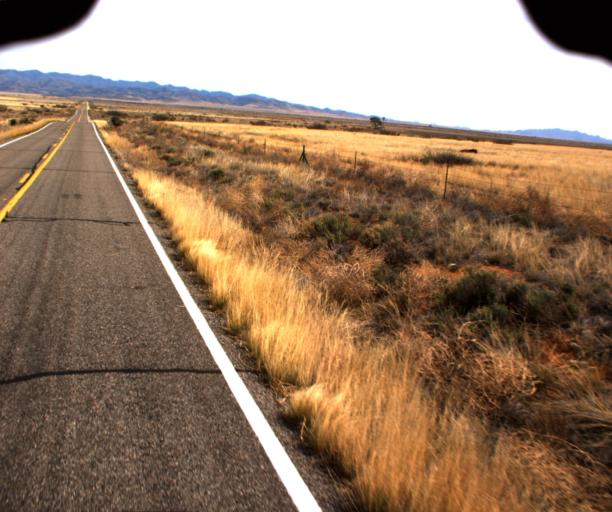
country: US
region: Arizona
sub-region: Cochise County
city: Willcox
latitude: 32.0798
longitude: -109.5206
